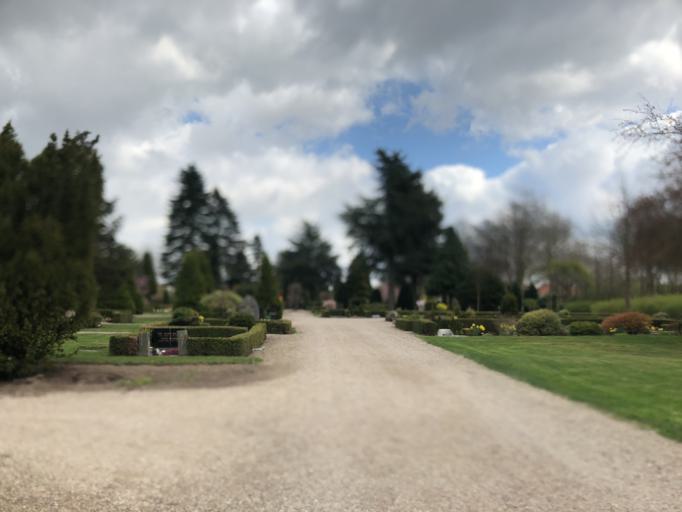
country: DK
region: Zealand
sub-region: Ringsted Kommune
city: Ringsted
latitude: 55.4413
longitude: 11.7947
